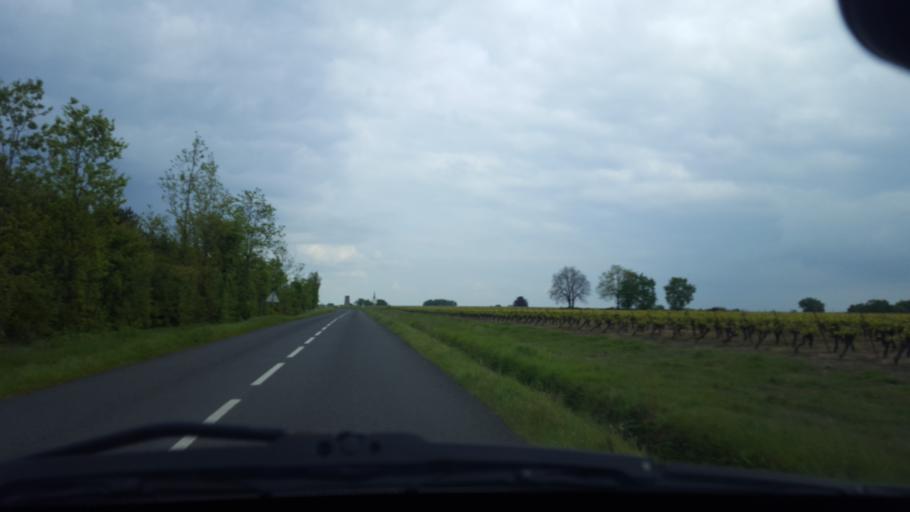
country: FR
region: Pays de la Loire
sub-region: Departement de la Loire-Atlantique
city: La Limouziniere
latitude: 47.0005
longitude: -1.6112
